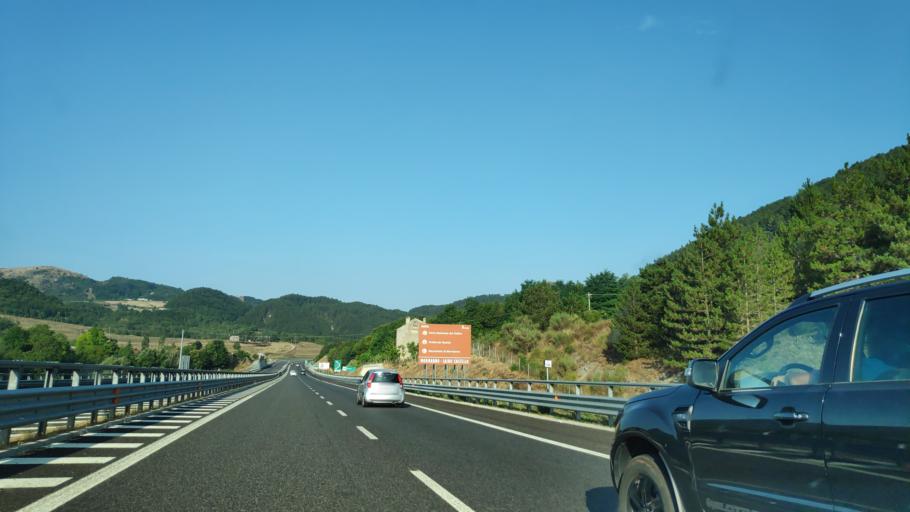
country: IT
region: Calabria
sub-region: Provincia di Cosenza
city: Mormanno
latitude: 39.8783
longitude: 16.0029
